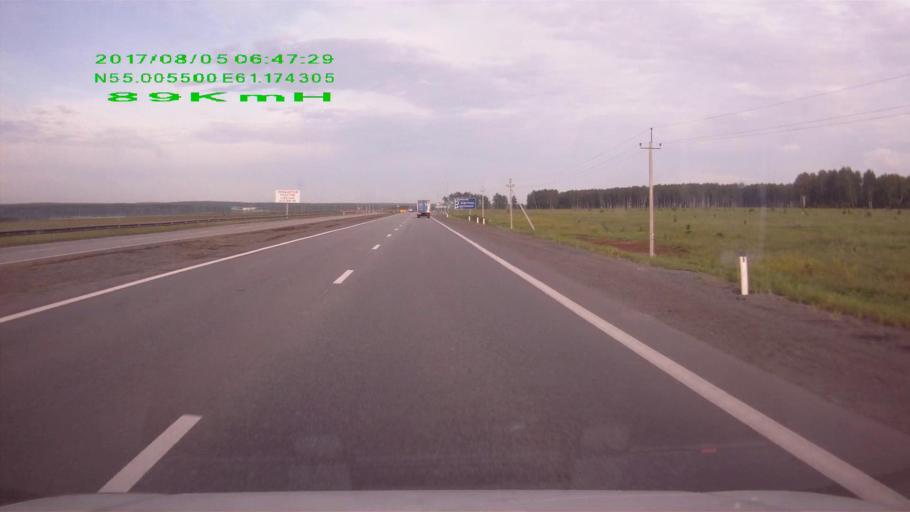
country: RU
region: Chelyabinsk
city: Poletayevo
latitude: 55.0055
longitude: 61.1743
